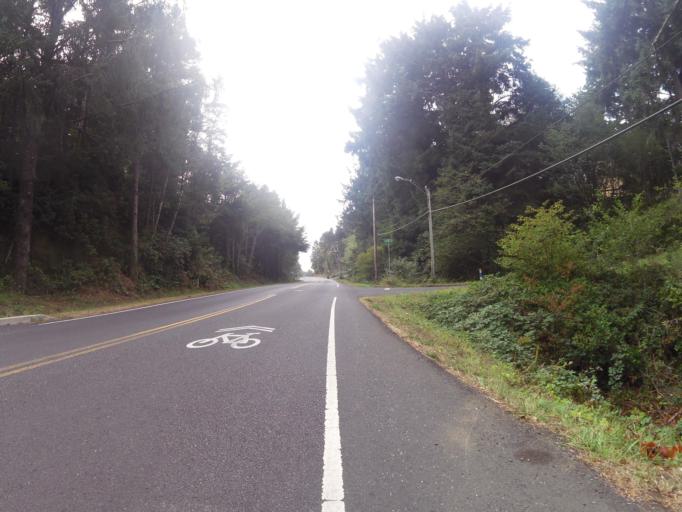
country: US
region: Oregon
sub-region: Lincoln County
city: Newport
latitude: 44.6558
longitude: -124.0562
